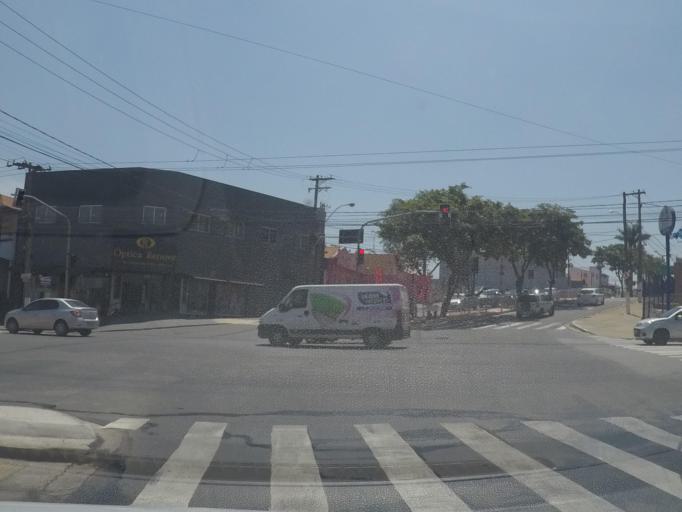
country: BR
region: Sao Paulo
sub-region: Hortolandia
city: Hortolandia
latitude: -22.8573
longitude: -47.2210
